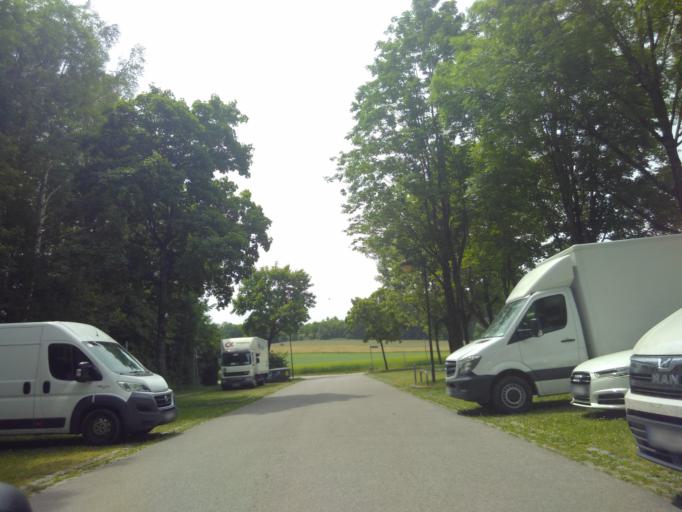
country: DE
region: Bavaria
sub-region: Upper Bavaria
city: Eichenau
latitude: 48.1672
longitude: 11.3124
